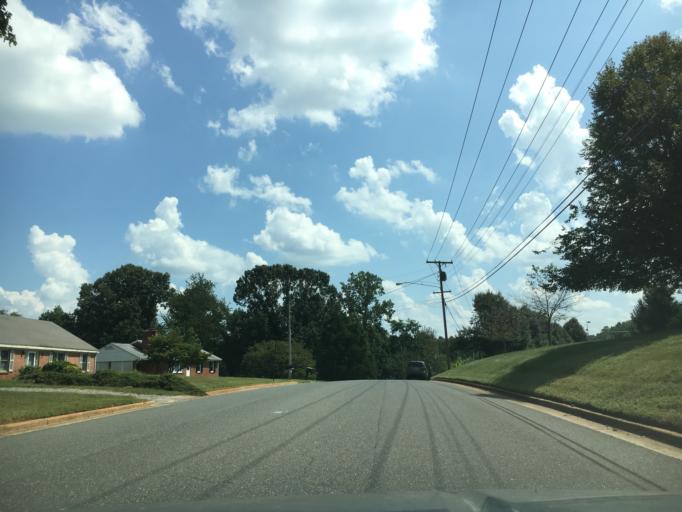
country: US
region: Virginia
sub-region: City of Lynchburg
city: West Lynchburg
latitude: 37.4191
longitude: -79.1704
